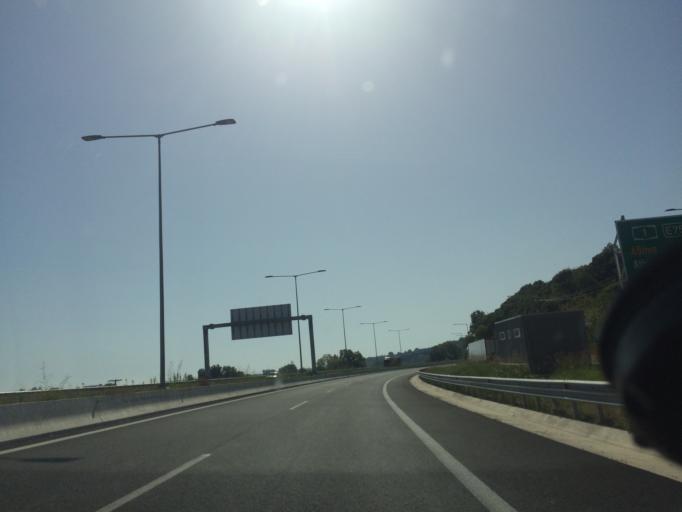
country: GR
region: Thessaly
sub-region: Nomos Larisis
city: Pyrgetos
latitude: 39.9755
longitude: 22.6357
